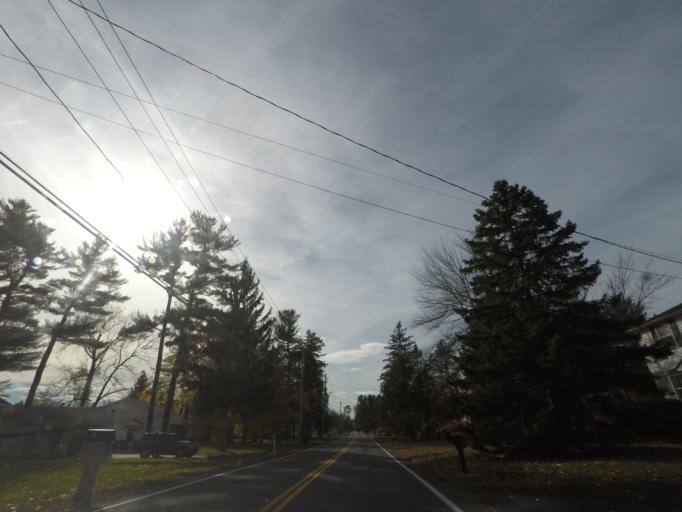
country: US
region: New York
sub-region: Schenectady County
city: Rotterdam
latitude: 42.7551
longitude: -73.9484
